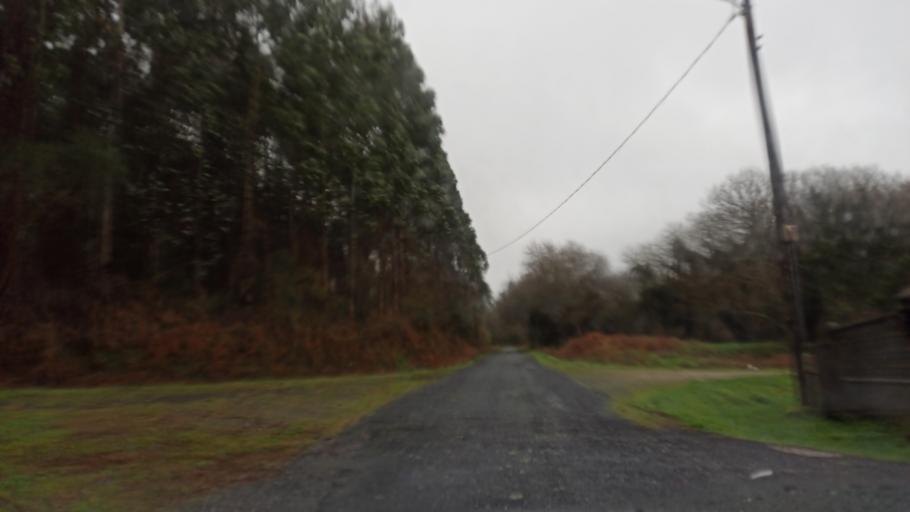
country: ES
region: Galicia
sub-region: Provincia da Coruna
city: Coiros
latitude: 43.1811
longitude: -8.1397
